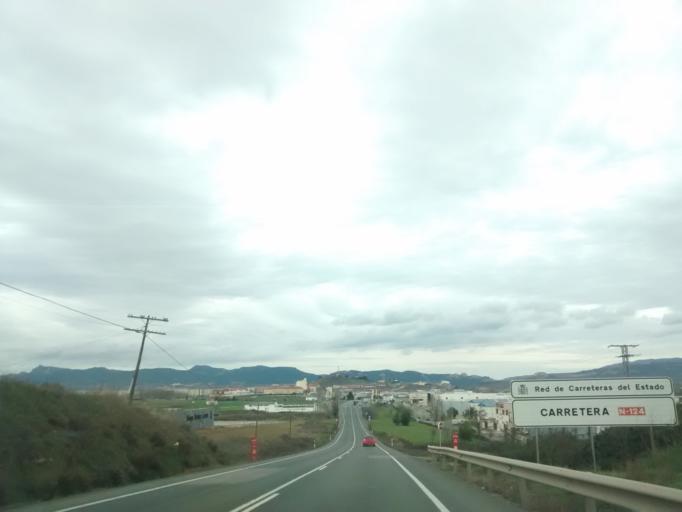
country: ES
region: La Rioja
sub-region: Provincia de La Rioja
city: Ollauri
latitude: 42.5564
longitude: -2.8356
